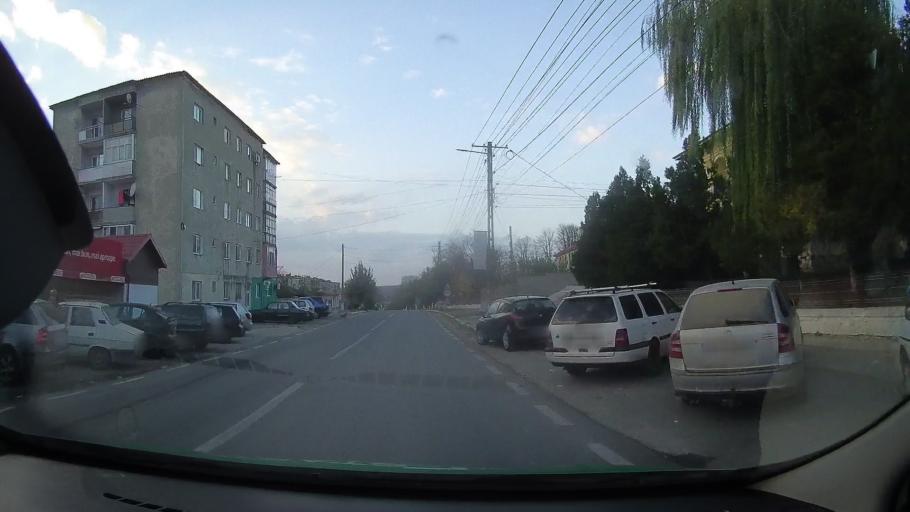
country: RO
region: Constanta
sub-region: Comuna Baneasa
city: Baneasa
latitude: 44.0656
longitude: 27.6974
